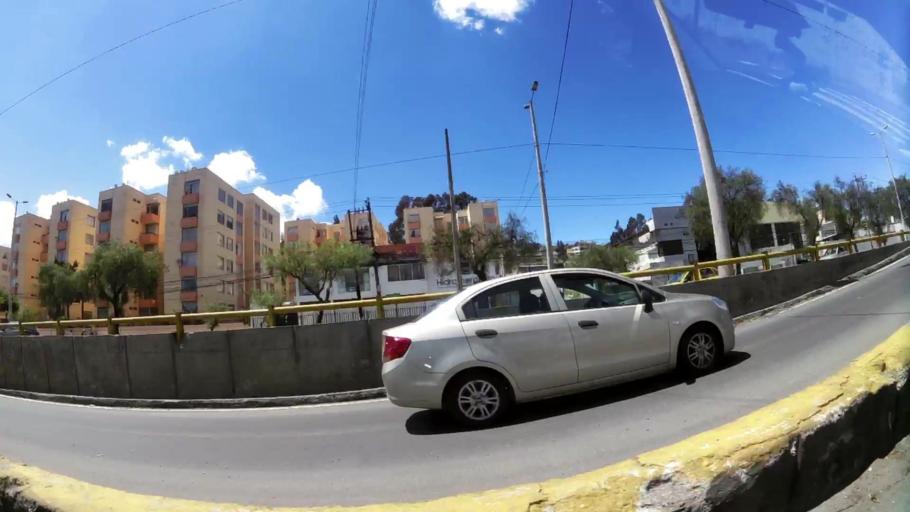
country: EC
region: Pichincha
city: Quito
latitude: -0.1202
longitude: -78.4802
